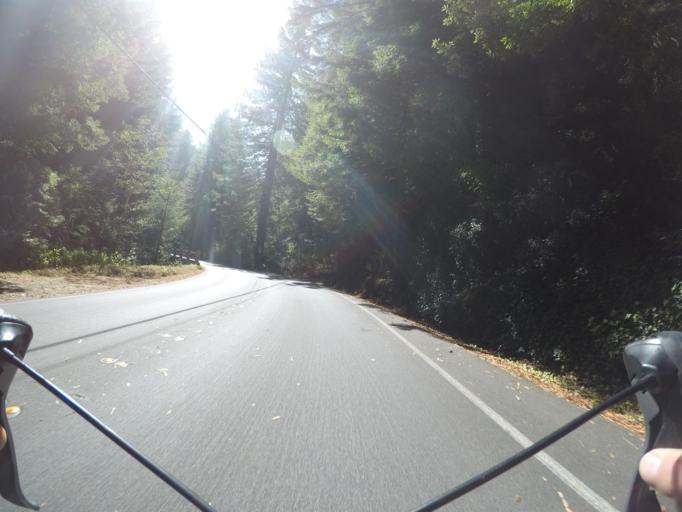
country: US
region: California
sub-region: San Mateo County
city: Portola Valley
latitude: 37.2679
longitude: -122.3148
